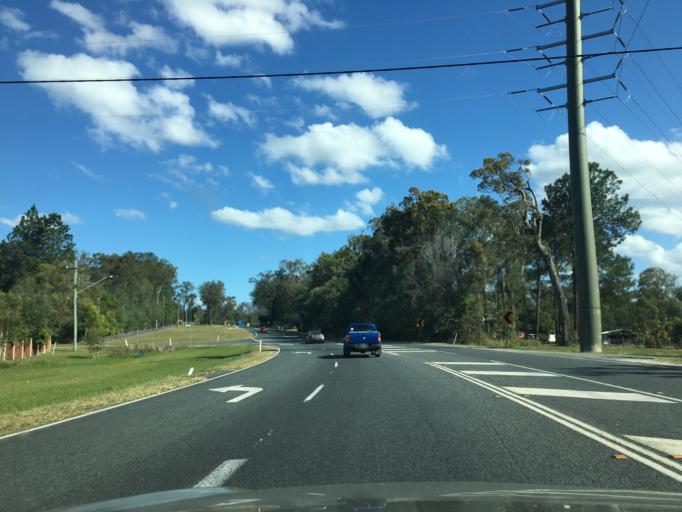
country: AU
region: Queensland
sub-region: Logan
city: Chambers Flat
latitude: -27.7832
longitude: 153.0988
